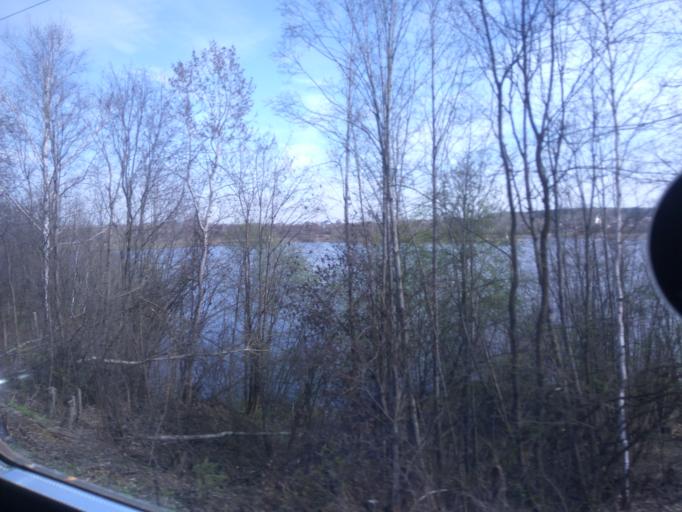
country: RU
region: Moskovskaya
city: Yermolino
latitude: 56.1499
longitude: 37.5050
